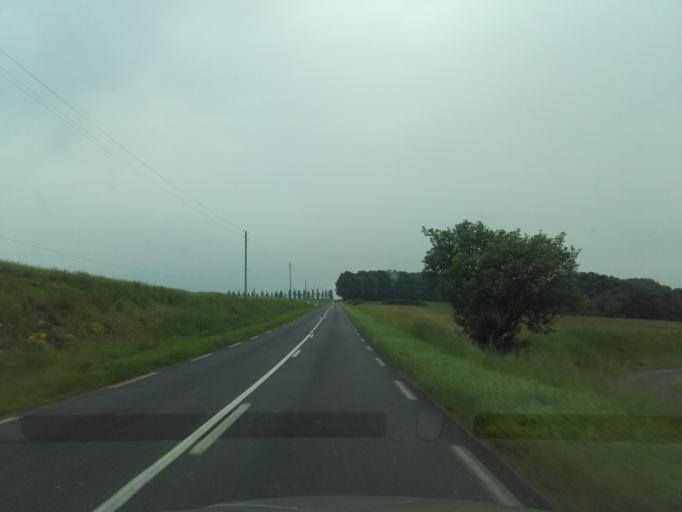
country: FR
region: Centre
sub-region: Departement d'Indre-et-Loire
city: Cerelles
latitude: 47.5350
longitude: 0.6923
